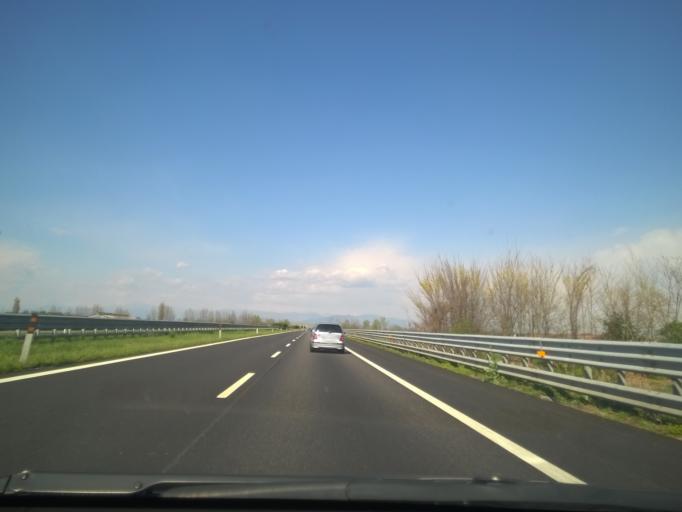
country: IT
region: Lombardy
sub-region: Provincia di Brescia
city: San Gervasio Bresciano
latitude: 45.3275
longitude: 10.1509
